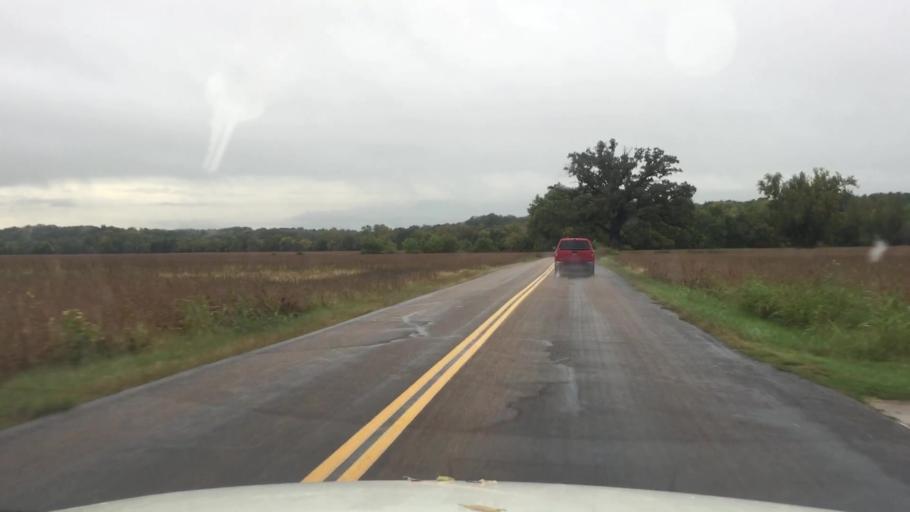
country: US
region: Missouri
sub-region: Boone County
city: Columbia
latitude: 38.8972
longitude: -92.4646
